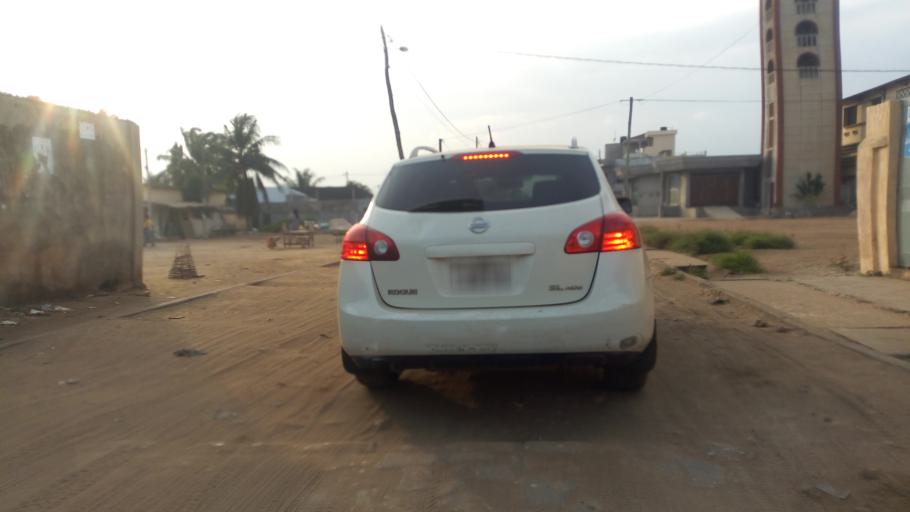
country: TG
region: Maritime
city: Lome
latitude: 6.1352
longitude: 1.2160
